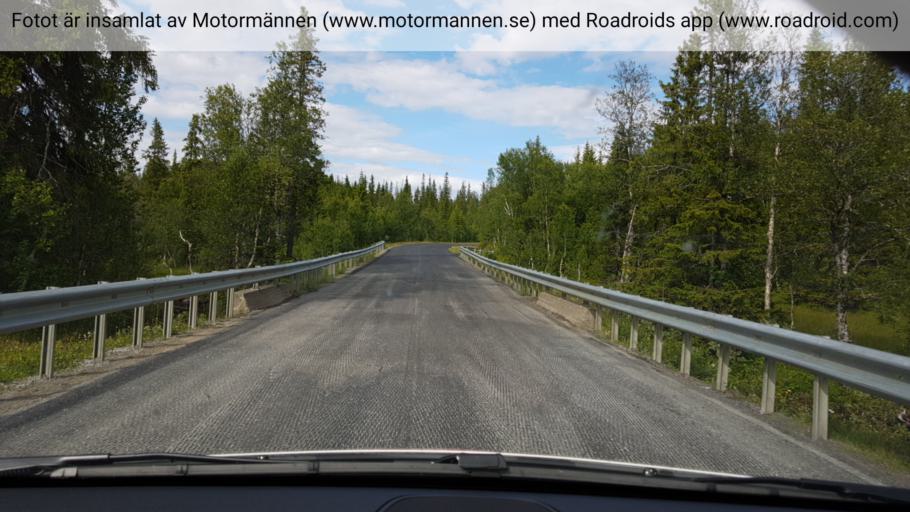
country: NO
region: Nord-Trondelag
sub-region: Meraker
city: Meraker
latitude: 63.6691
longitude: 12.2510
